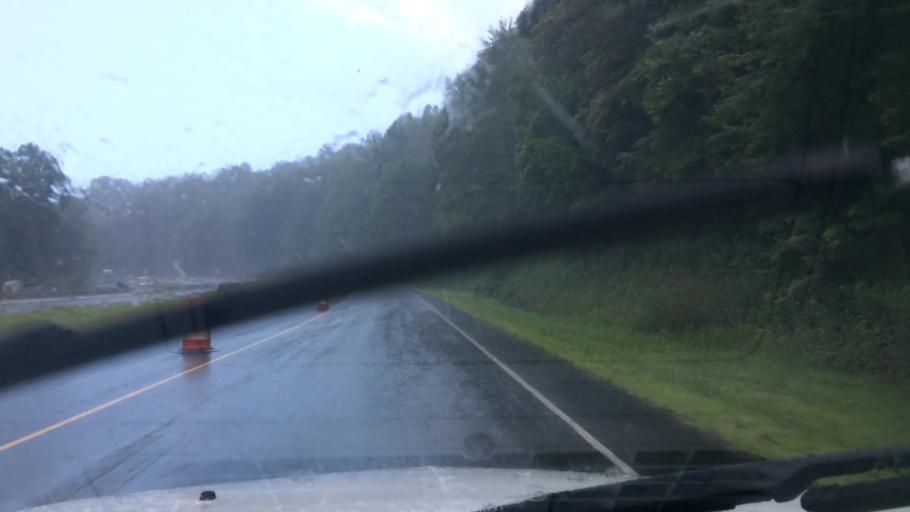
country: US
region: North Carolina
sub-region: Wilkes County
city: Millers Creek
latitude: 36.2021
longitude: -81.4336
